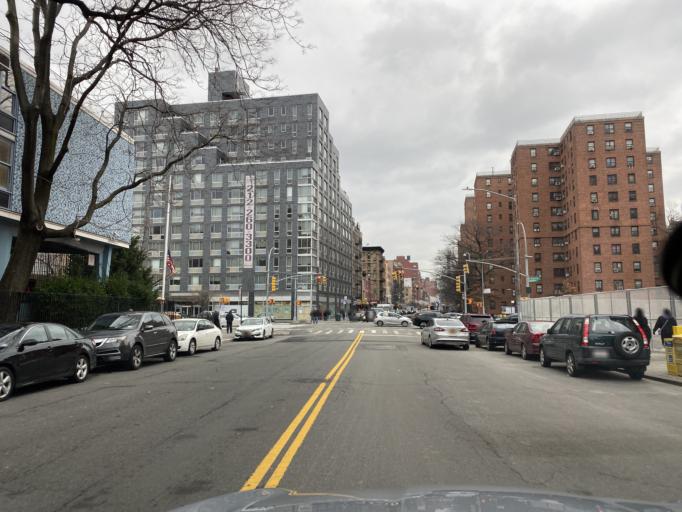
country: US
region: New York
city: New York City
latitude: 40.7194
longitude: -73.9790
